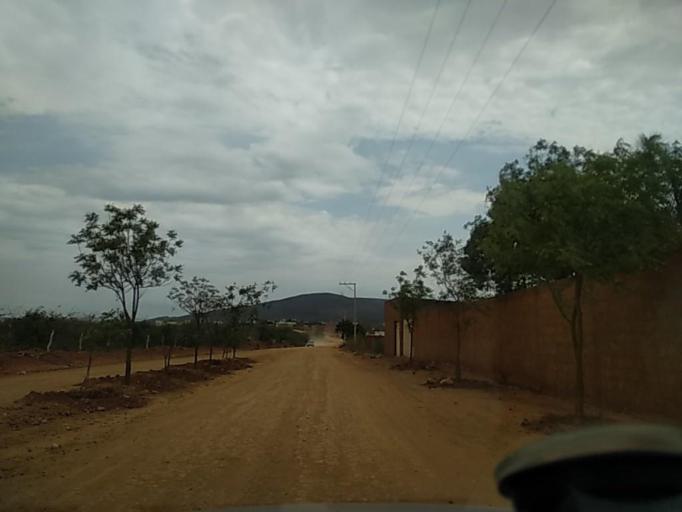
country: BR
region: Bahia
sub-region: Caetite
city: Caetite
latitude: -14.0472
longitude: -42.4731
